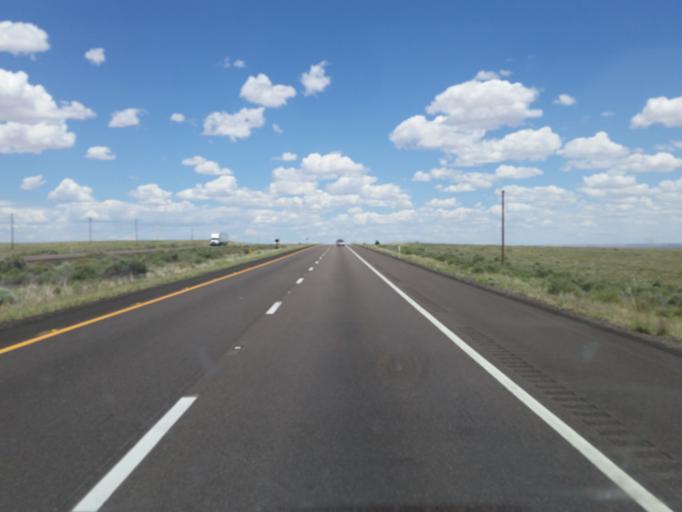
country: US
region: Arizona
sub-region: Navajo County
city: Holbrook
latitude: 34.9866
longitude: -110.0202
